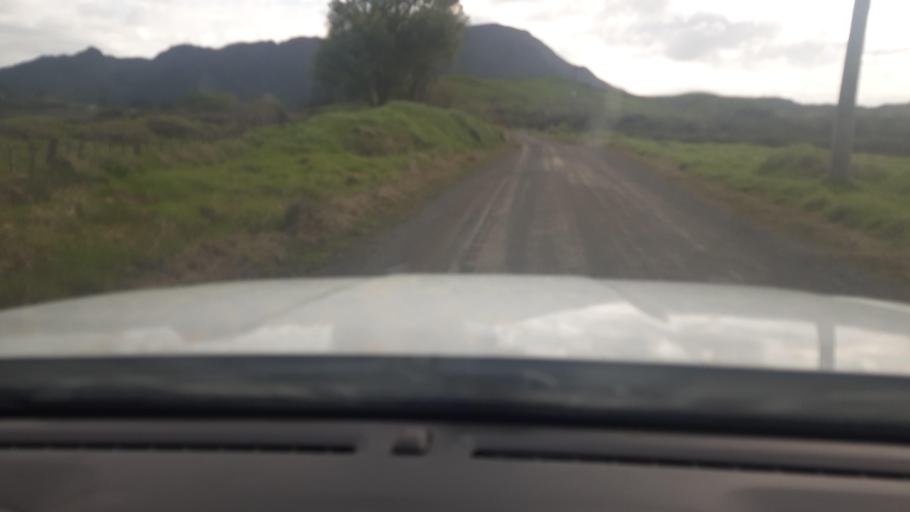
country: NZ
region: Northland
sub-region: Far North District
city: Ahipara
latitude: -35.2580
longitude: 173.2028
